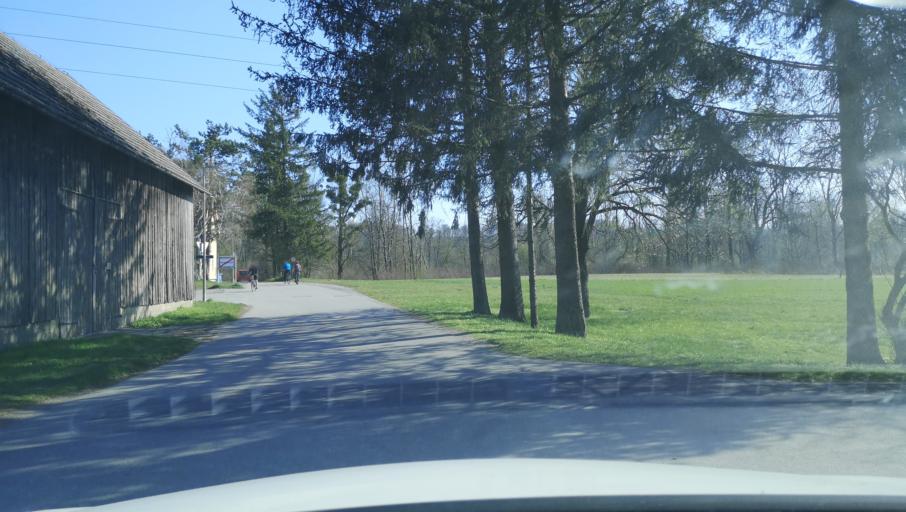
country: AT
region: Lower Austria
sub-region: Politischer Bezirk Melk
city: Blindenmarkt
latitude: 48.1215
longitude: 14.9883
